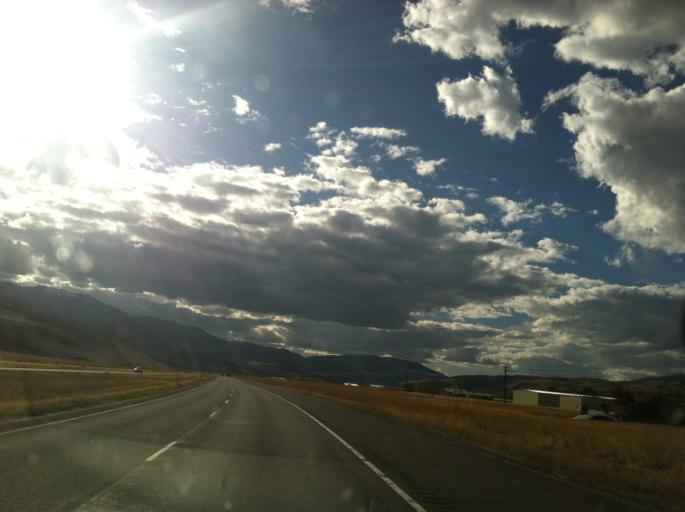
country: US
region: Montana
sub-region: Deer Lodge County
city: Anaconda
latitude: 46.1281
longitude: -112.9014
